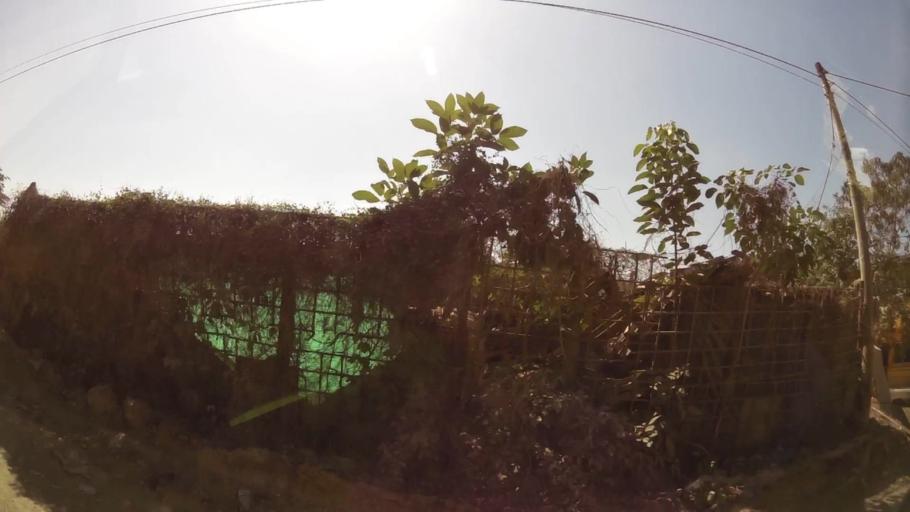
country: CO
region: Bolivar
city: Cartagena
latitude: 10.3580
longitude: -75.4897
